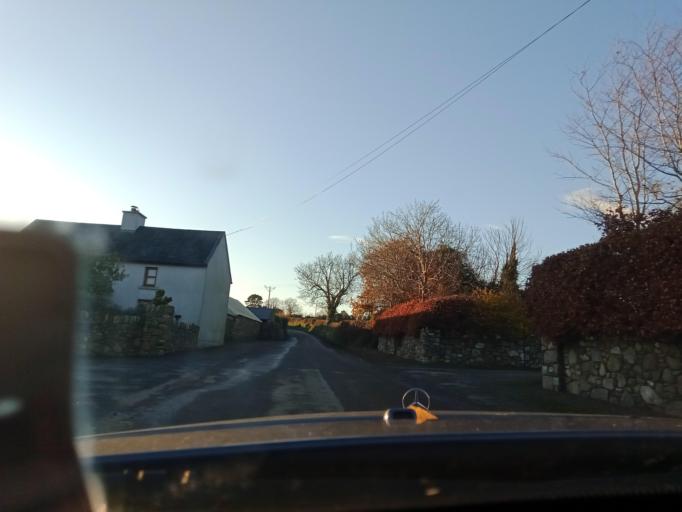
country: IE
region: Leinster
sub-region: Loch Garman
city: New Ross
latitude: 52.3898
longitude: -6.9795
